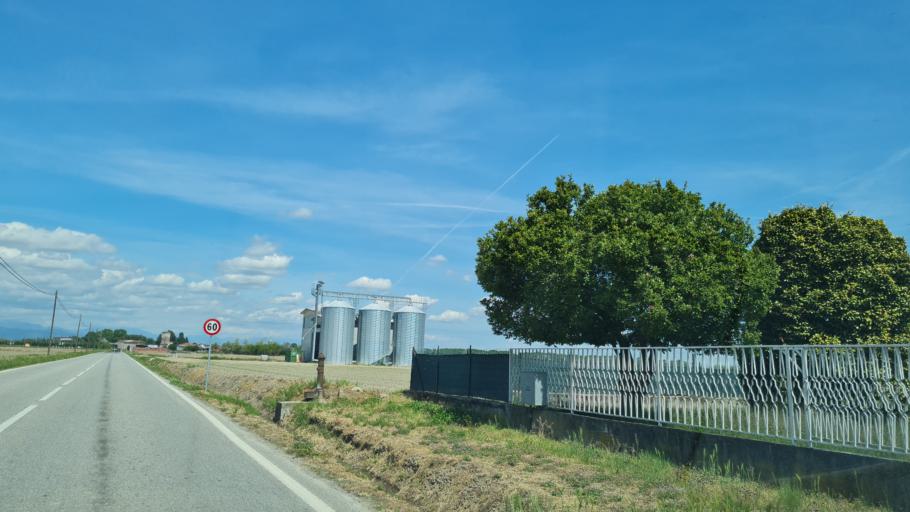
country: IT
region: Piedmont
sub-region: Provincia di Novara
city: Vicolungo
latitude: 45.4851
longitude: 8.4599
